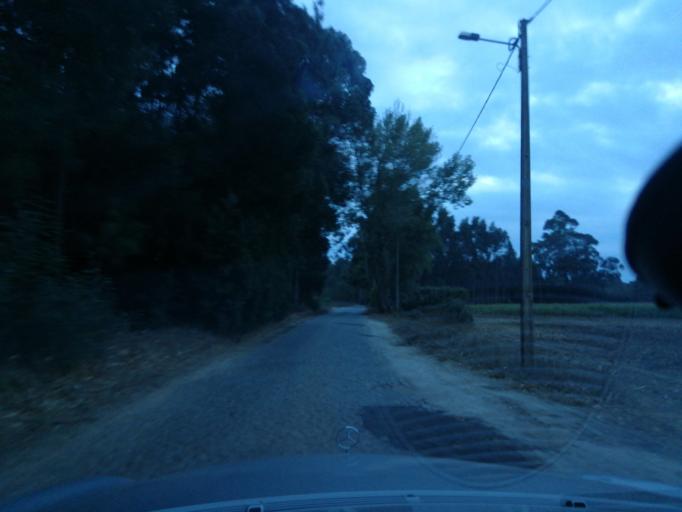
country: PT
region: Aveiro
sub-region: Estarreja
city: Estarreja
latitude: 40.7630
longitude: -8.6001
